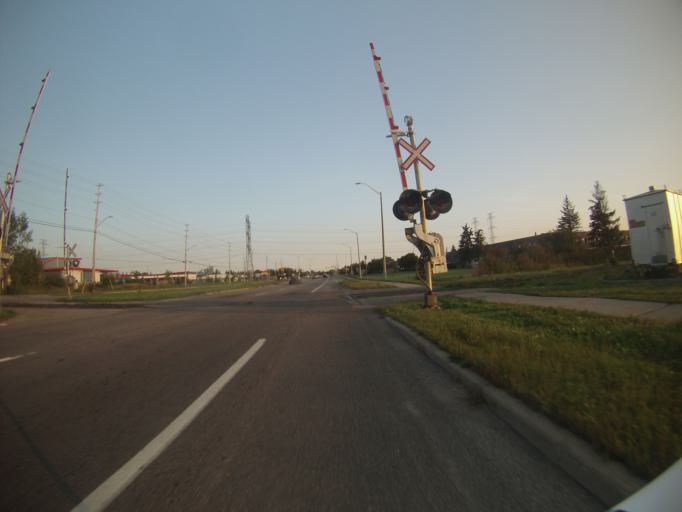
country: CA
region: Ontario
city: Ottawa
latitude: 45.3763
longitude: -75.6256
